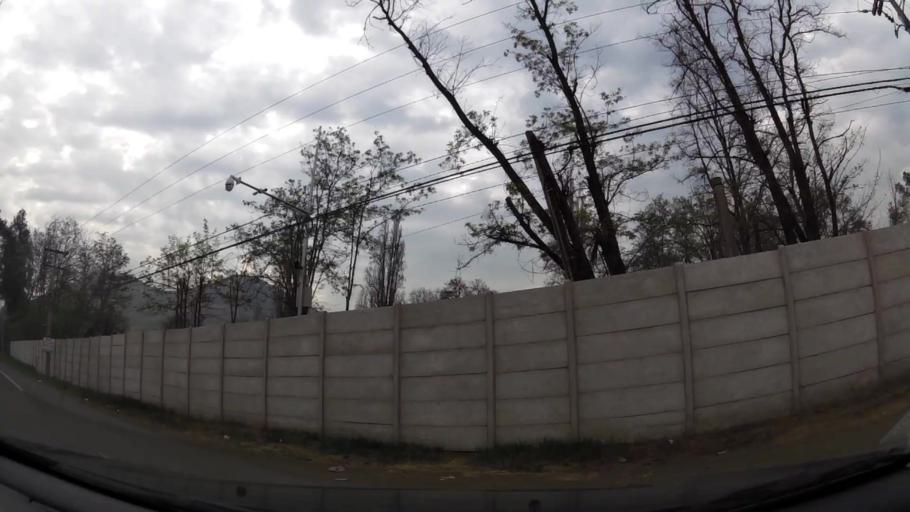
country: CL
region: Santiago Metropolitan
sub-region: Provincia de Chacabuco
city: Chicureo Abajo
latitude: -33.2451
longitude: -70.6753
